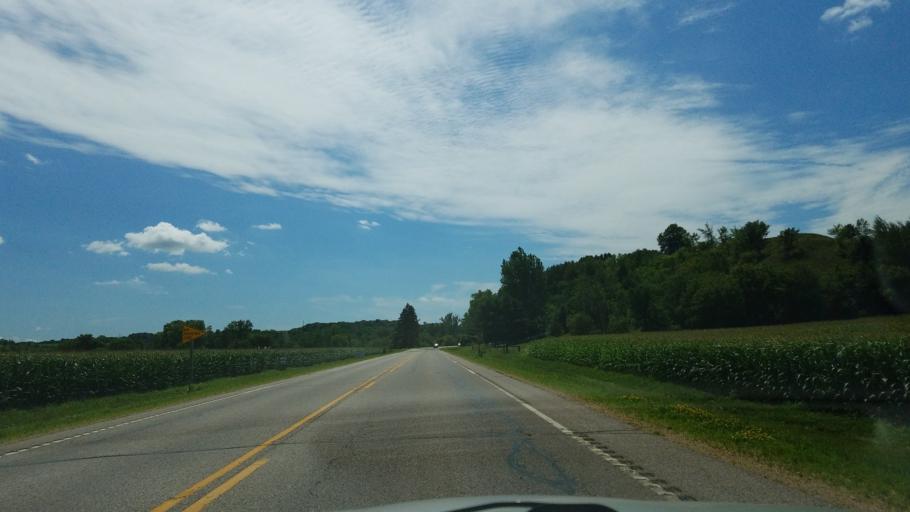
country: US
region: Wisconsin
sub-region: Saint Croix County
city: Glenwood City
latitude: 45.0420
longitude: -92.1752
